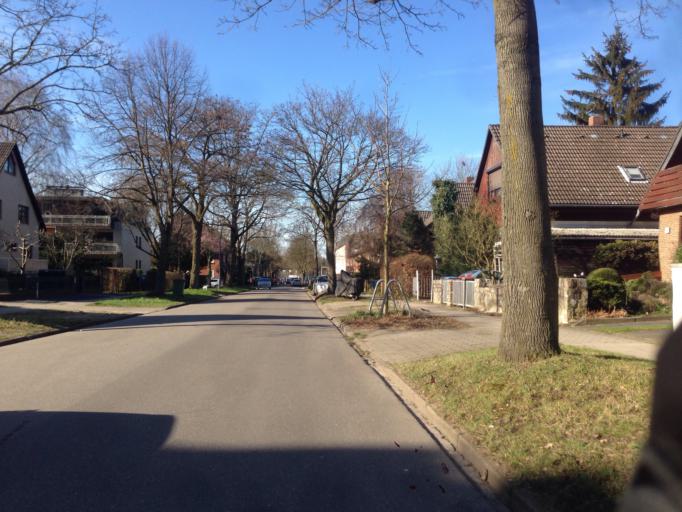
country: DE
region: Hamburg
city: Wandsbek
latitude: 53.5716
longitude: 10.0981
